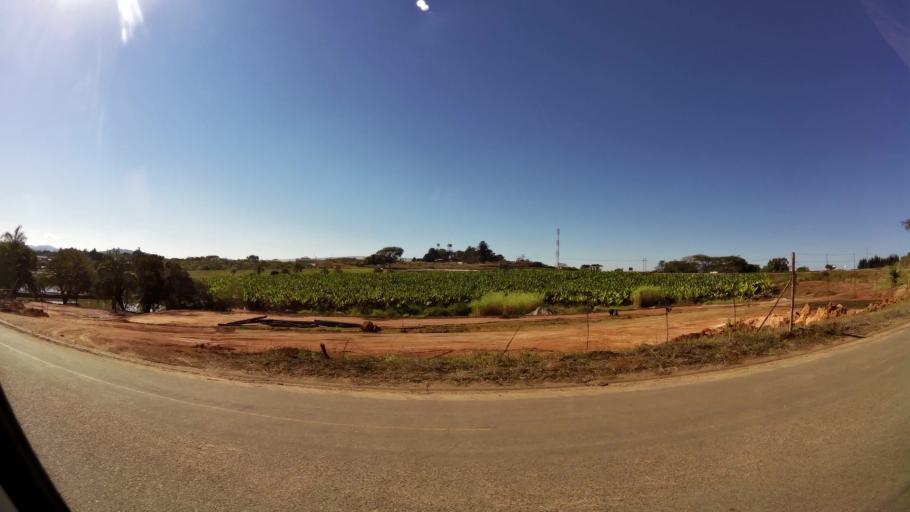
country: ZA
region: Limpopo
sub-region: Mopani District Municipality
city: Tzaneen
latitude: -23.8356
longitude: 30.1331
